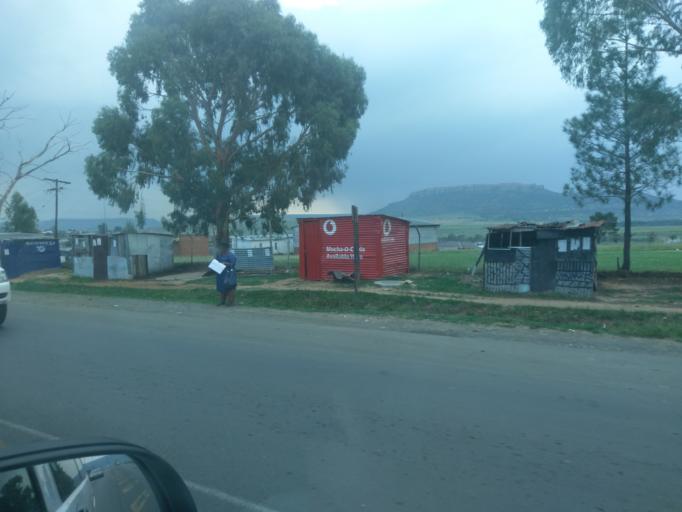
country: LS
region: Maseru
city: Maseru
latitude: -29.2689
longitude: 27.5377
